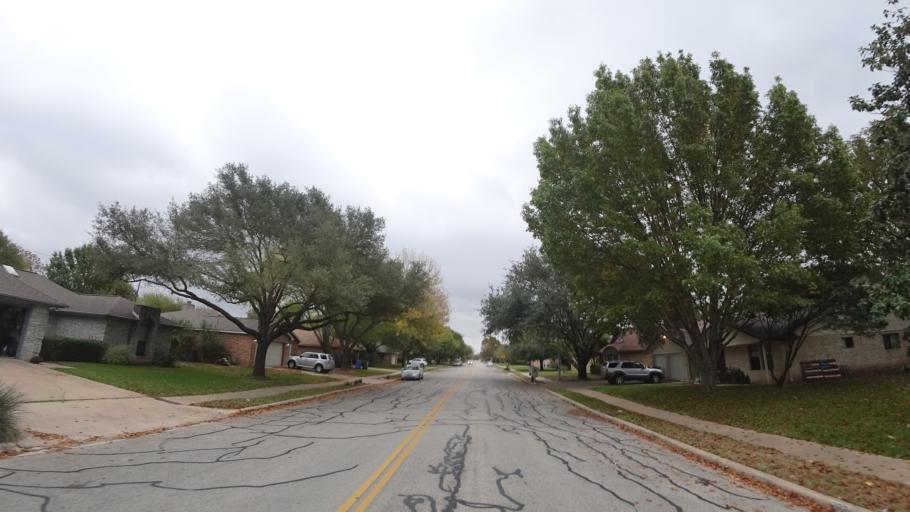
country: US
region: Texas
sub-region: Travis County
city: Pflugerville
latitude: 30.4455
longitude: -97.6161
